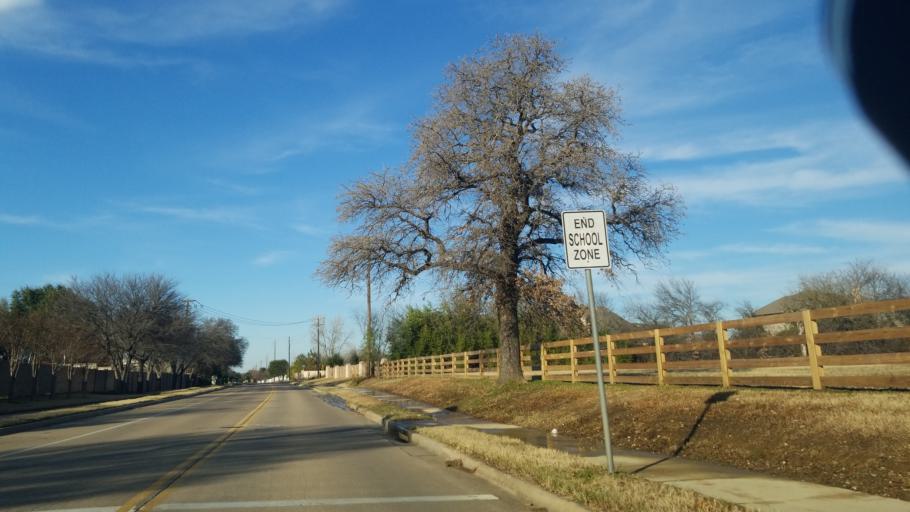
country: US
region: Texas
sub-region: Denton County
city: Corinth
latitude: 33.1500
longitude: -97.0789
